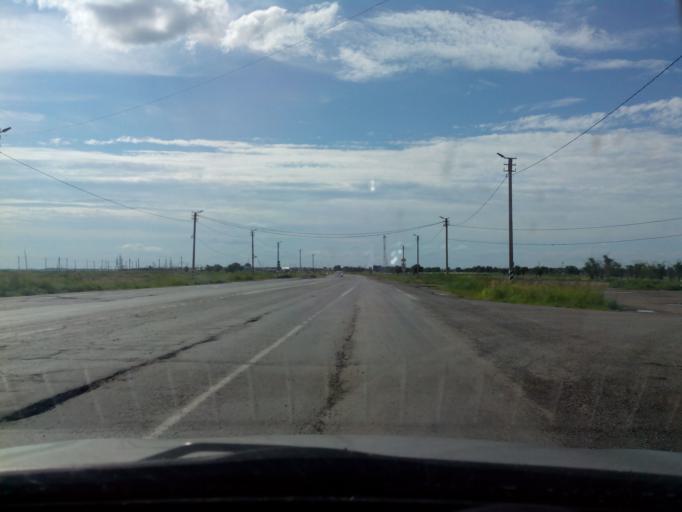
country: RU
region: Astrakhan
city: Kapustin Yar
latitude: 48.5625
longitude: 45.7958
